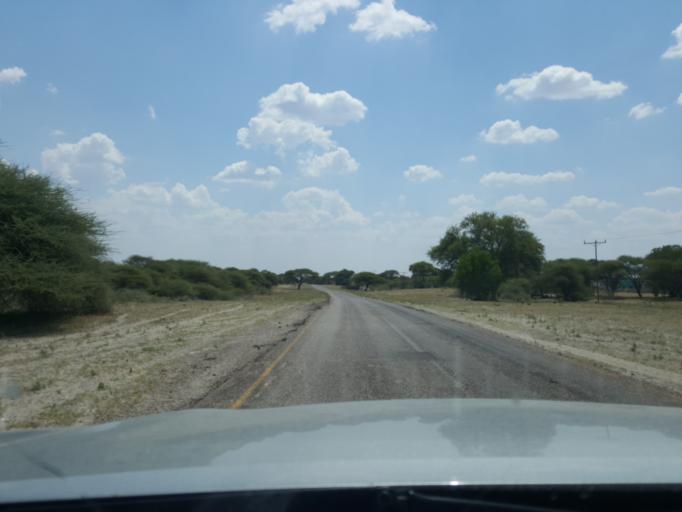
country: BW
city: Tsau
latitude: -20.1885
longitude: 22.4749
